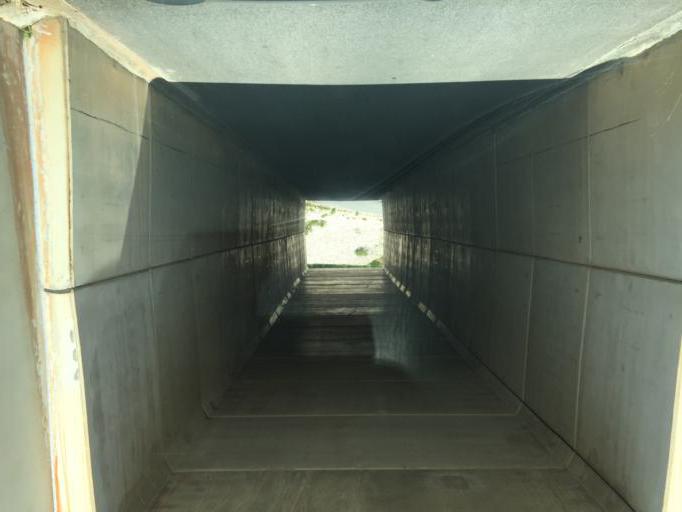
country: PT
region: Santarem
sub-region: Ourem
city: Ourem
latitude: 39.6748
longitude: -8.5728
